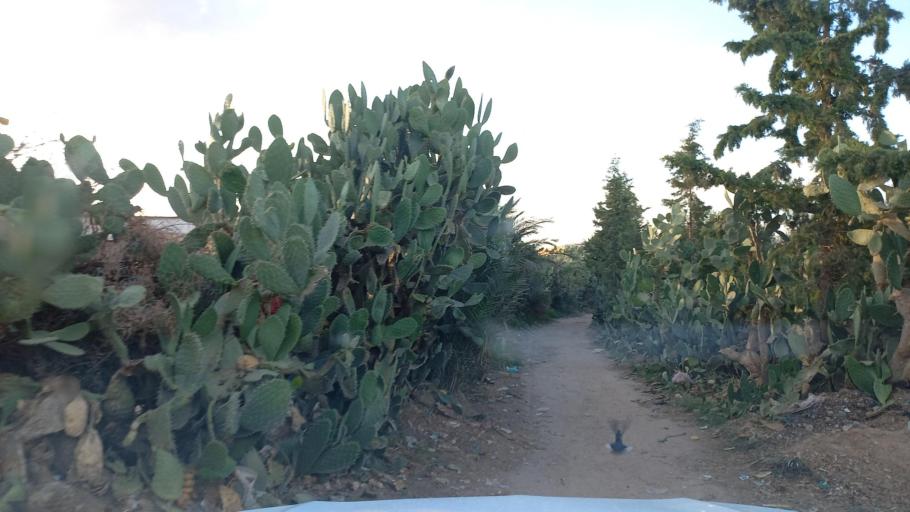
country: TN
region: Al Qasrayn
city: Sbiba
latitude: 35.3788
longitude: 9.0540
